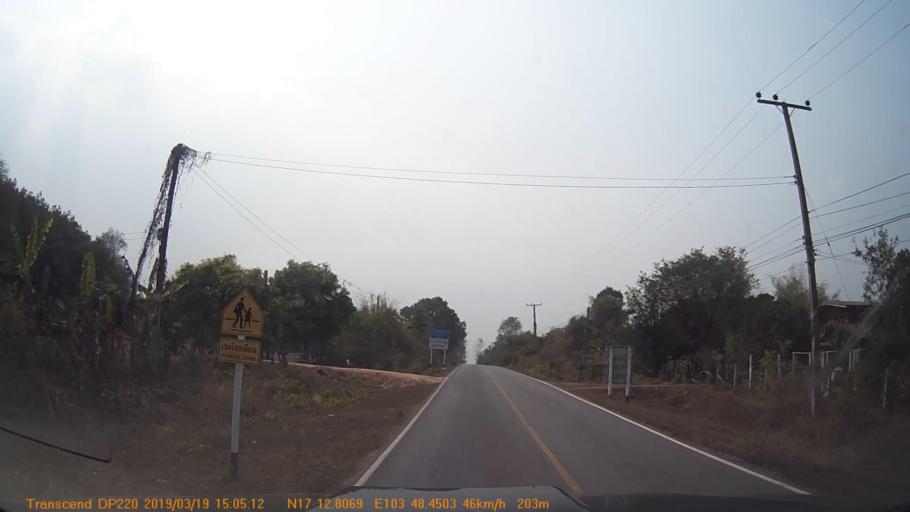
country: TH
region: Sakon Nakhon
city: Nikhom Nam Un
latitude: 17.2136
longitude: 103.8073
